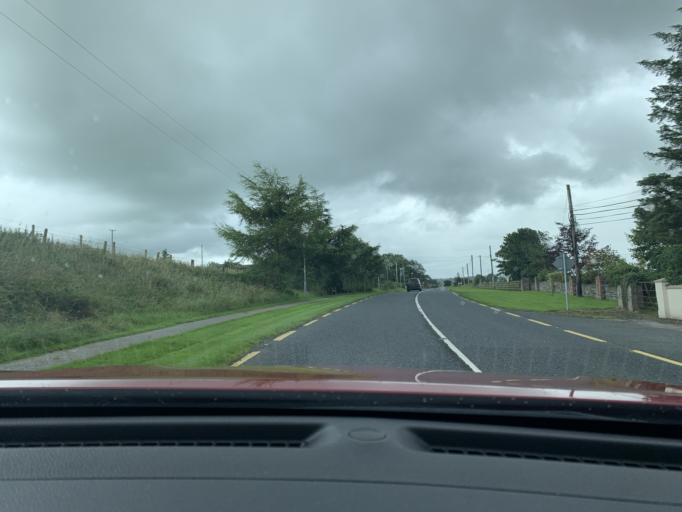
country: IE
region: Ulster
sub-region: County Donegal
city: Raphoe
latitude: 54.8005
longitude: -7.5780
